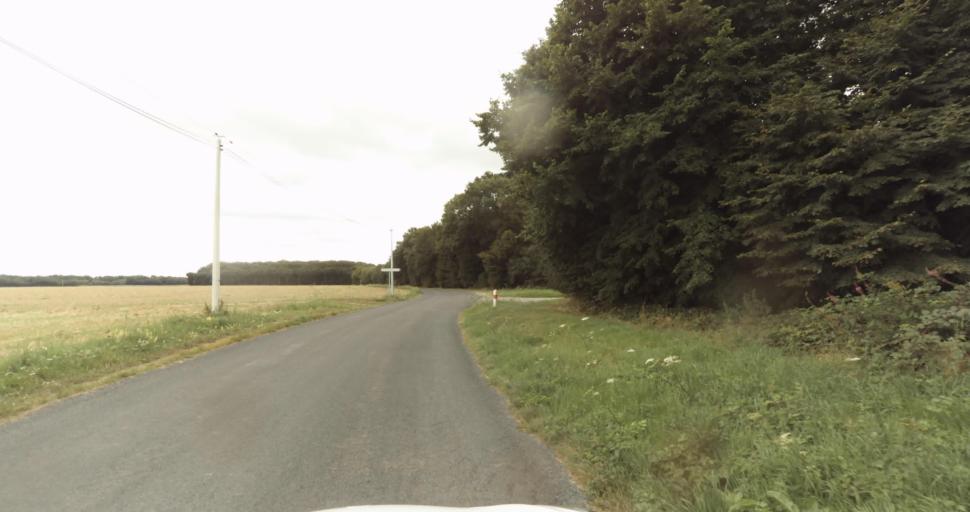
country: FR
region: Haute-Normandie
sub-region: Departement de l'Eure
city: La Madeleine-de-Nonancourt
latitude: 48.8218
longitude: 1.2142
